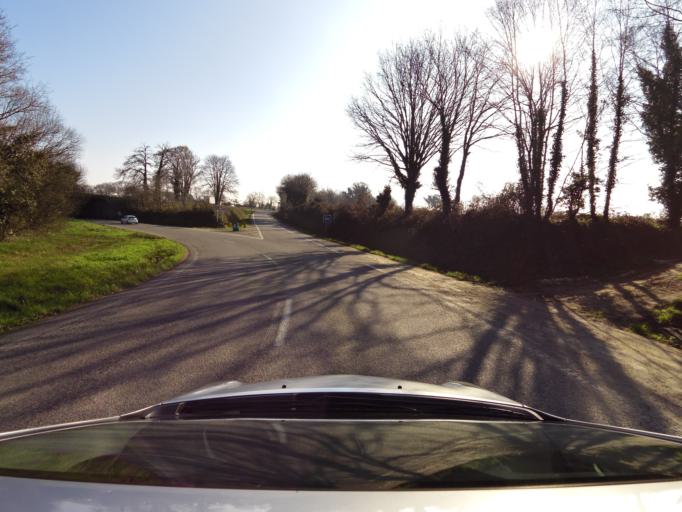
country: FR
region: Brittany
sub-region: Departement du Morbihan
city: Caudan
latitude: 47.7917
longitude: -3.3109
